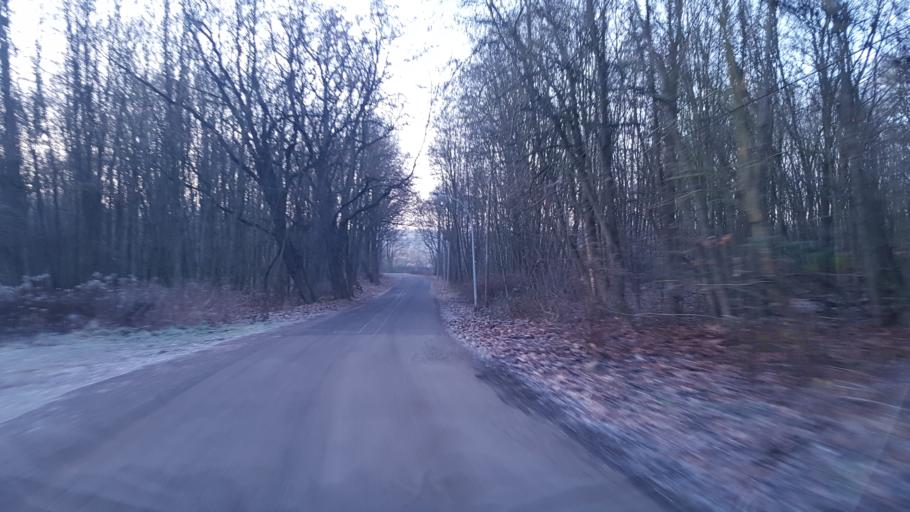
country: DE
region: Brandenburg
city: Schipkau
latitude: 51.5485
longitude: 13.8856
